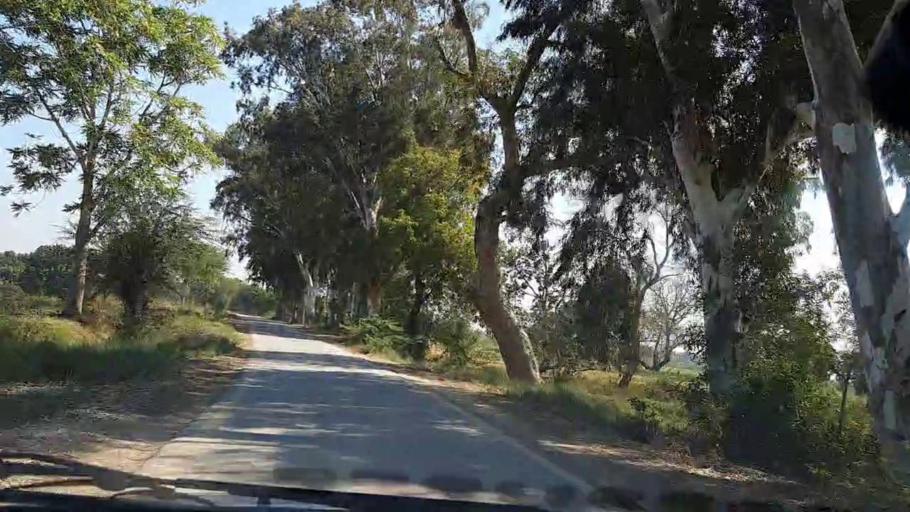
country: PK
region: Sindh
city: Mirpur Khas
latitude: 25.4712
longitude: 69.0172
